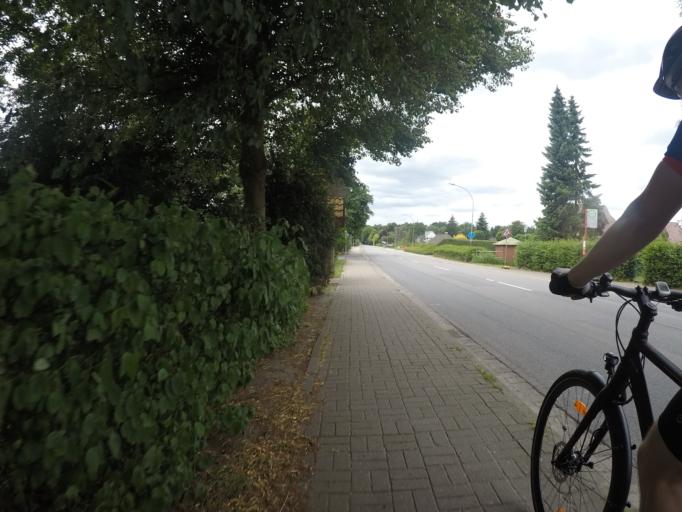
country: DE
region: Lower Saxony
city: Grossenworden
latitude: 53.6789
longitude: 9.2621
